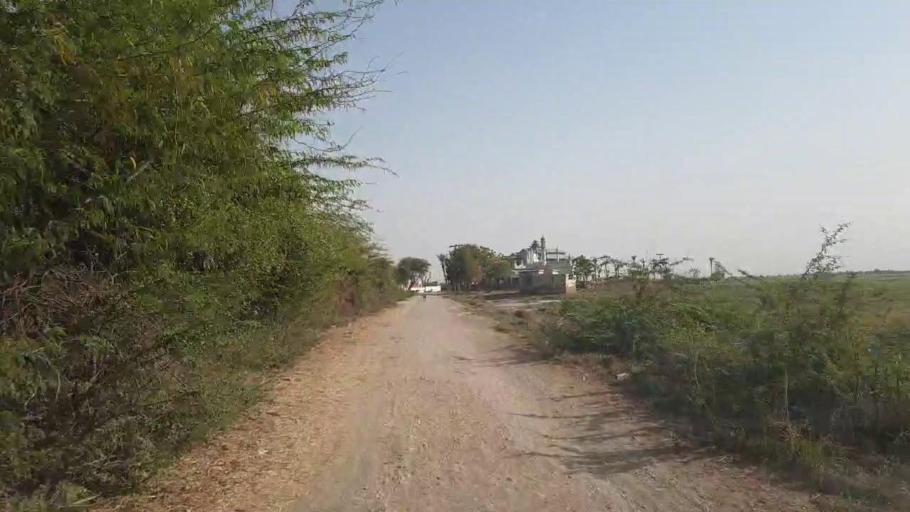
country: PK
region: Sindh
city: Dhoro Naro
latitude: 25.4653
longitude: 69.5507
